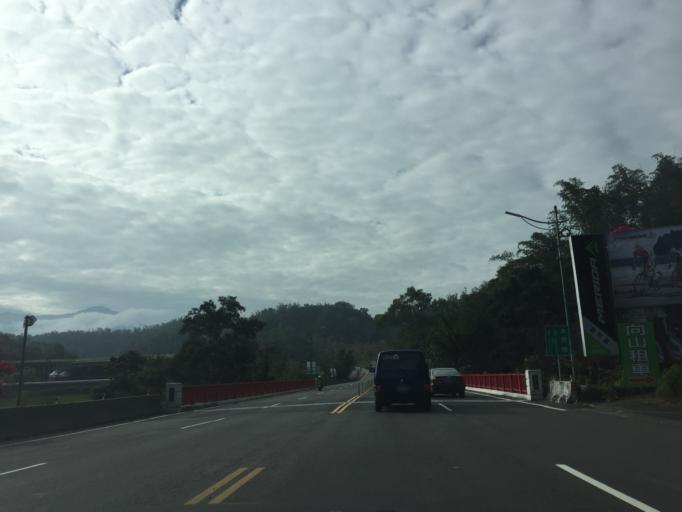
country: TW
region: Taiwan
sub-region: Nantou
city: Puli
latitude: 23.8543
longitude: 120.9018
